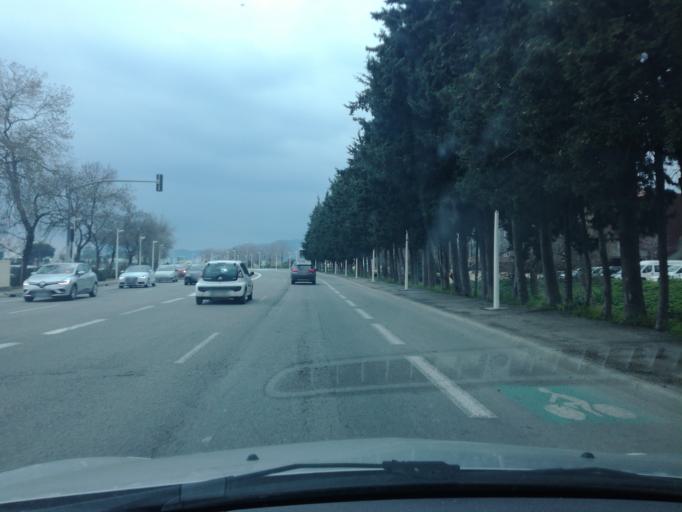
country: FR
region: Provence-Alpes-Cote d'Azur
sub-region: Departement des Alpes-Maritimes
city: Mandelieu-la-Napoule
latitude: 43.5528
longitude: 6.9629
